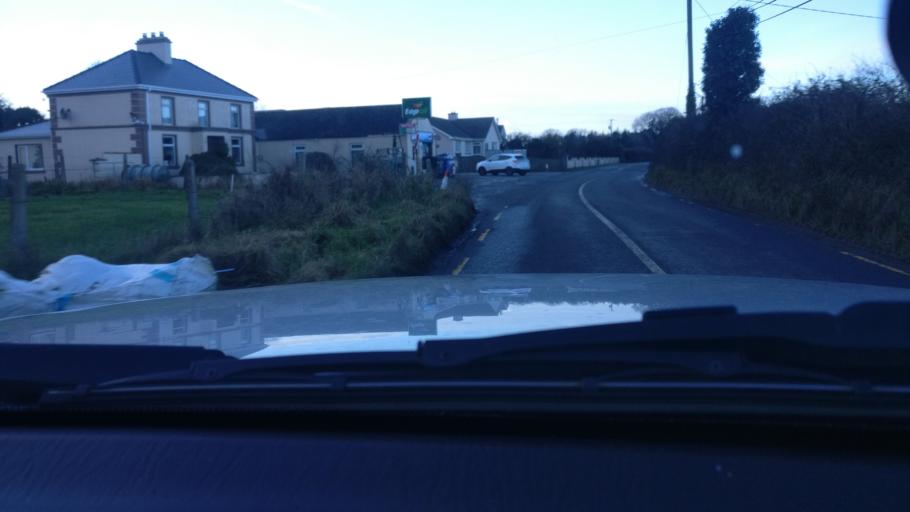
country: IE
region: Connaught
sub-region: County Galway
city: Loughrea
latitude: 53.2250
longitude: -8.4049
